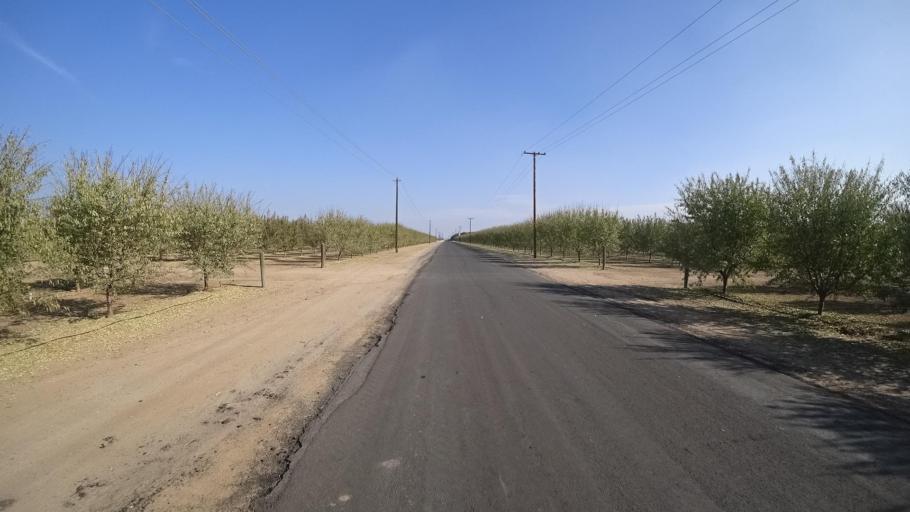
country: US
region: California
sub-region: Kern County
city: McFarland
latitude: 35.6311
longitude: -119.2000
